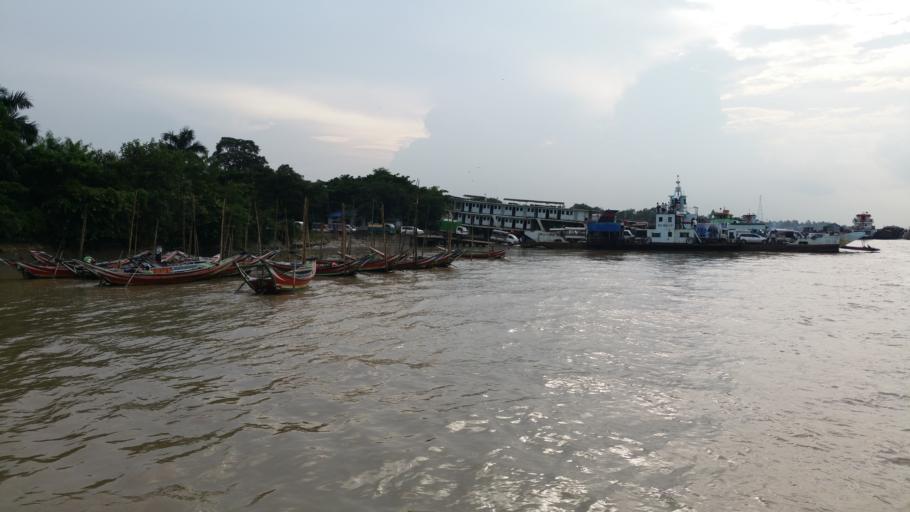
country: MM
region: Yangon
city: Yangon
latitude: 16.7629
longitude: 96.1561
